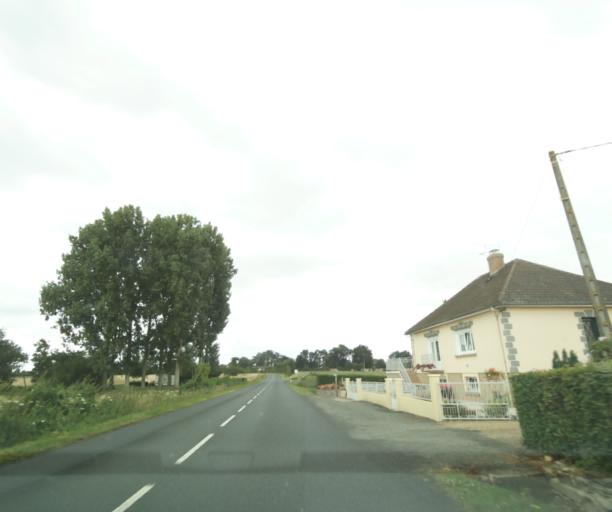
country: FR
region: Pays de la Loire
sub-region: Departement de la Sarthe
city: Precigne
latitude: 47.7785
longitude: -0.3187
